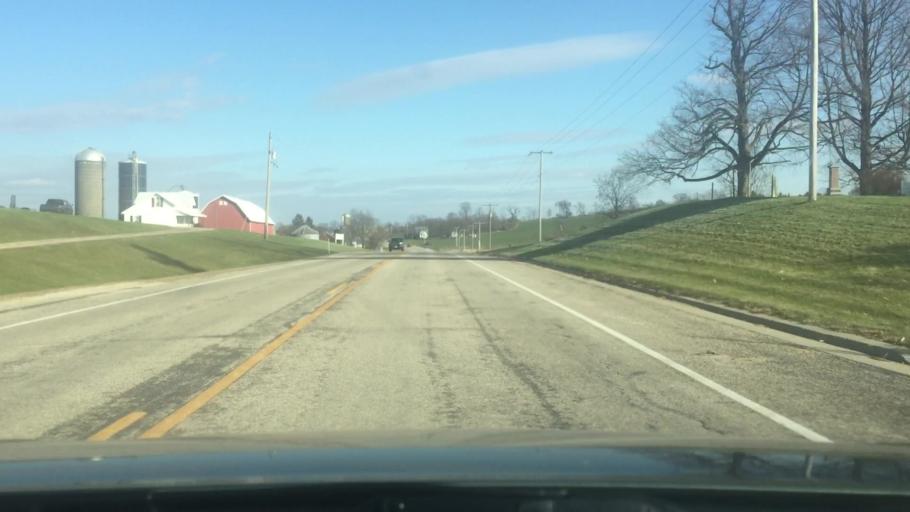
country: US
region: Wisconsin
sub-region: Jefferson County
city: Palmyra
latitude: 42.9326
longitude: -88.6559
